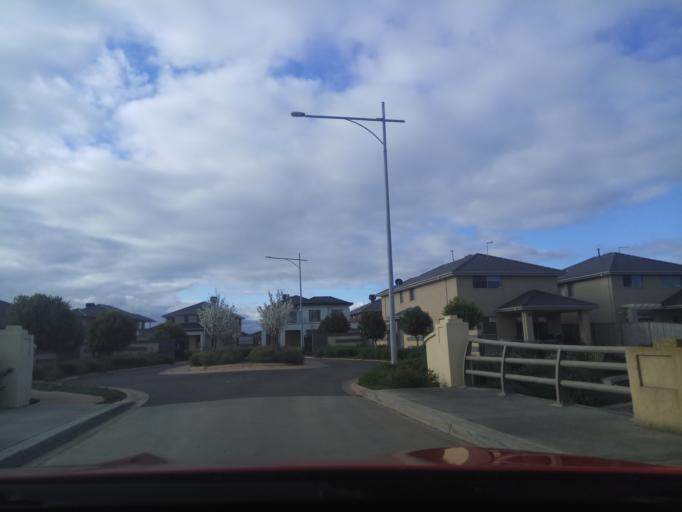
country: AU
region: Victoria
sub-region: Hobsons Bay
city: Altona Meadows
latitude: -37.9021
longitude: 144.7704
